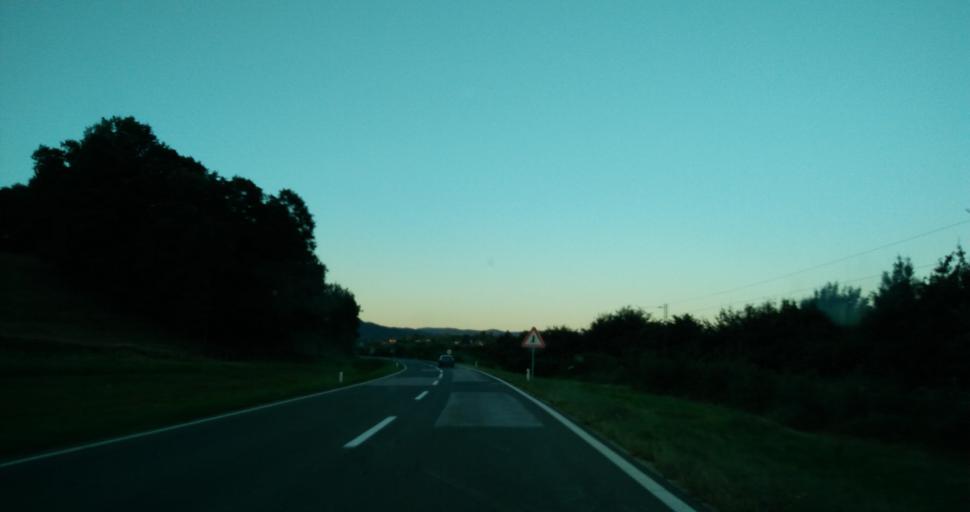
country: BA
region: Republika Srpska
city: Svodna
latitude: 45.0114
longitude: 16.6061
